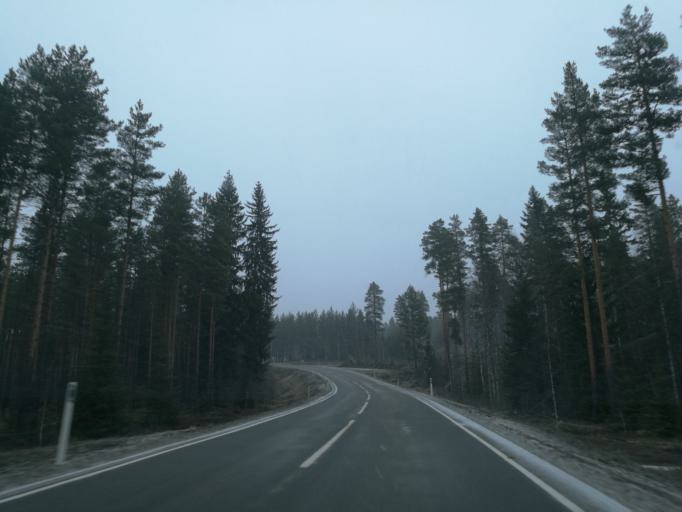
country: NO
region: Hedmark
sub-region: Asnes
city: Flisa
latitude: 60.6904
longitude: 12.3040
